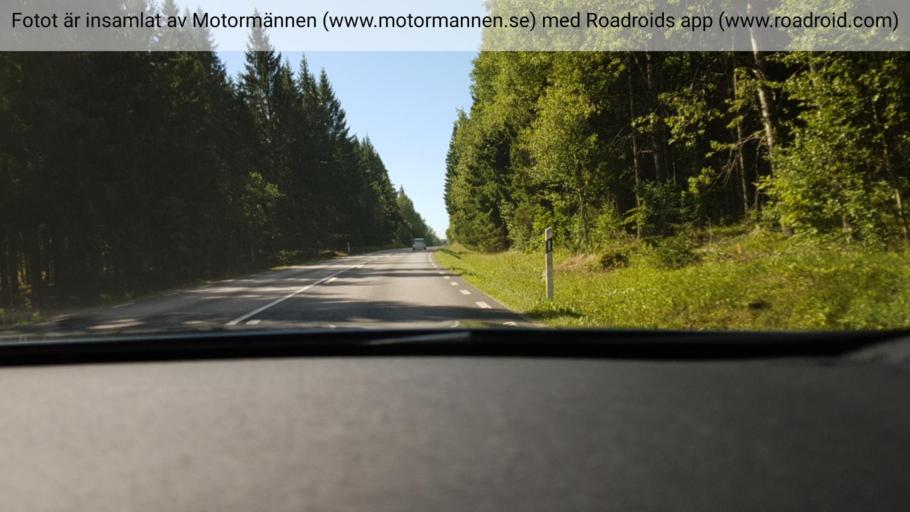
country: SE
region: Joenkoeping
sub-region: Mullsjo Kommun
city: Mullsjoe
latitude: 58.0661
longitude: 13.8079
